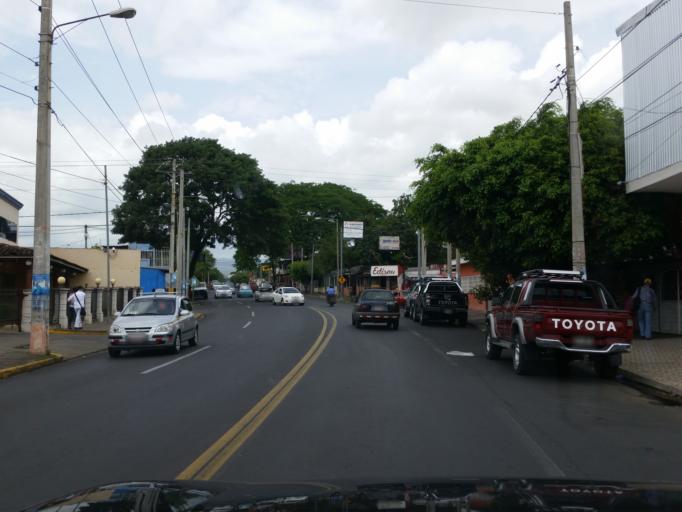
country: NI
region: Managua
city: Managua
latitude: 12.1470
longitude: -86.2506
